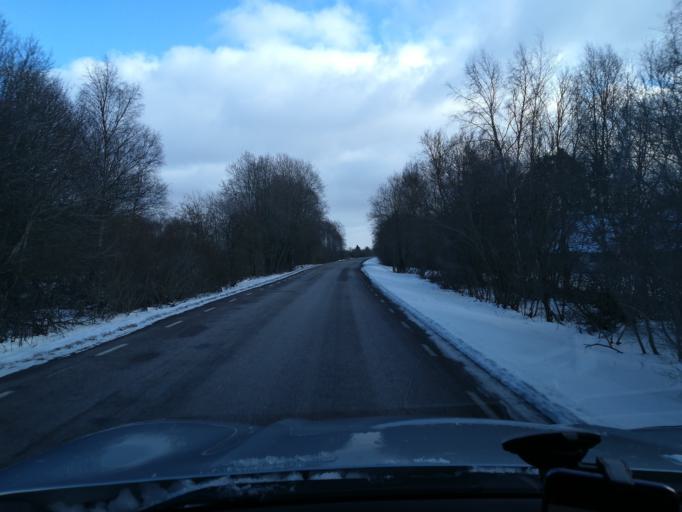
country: EE
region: Harju
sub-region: Keila linn
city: Keila
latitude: 59.4395
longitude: 24.3945
